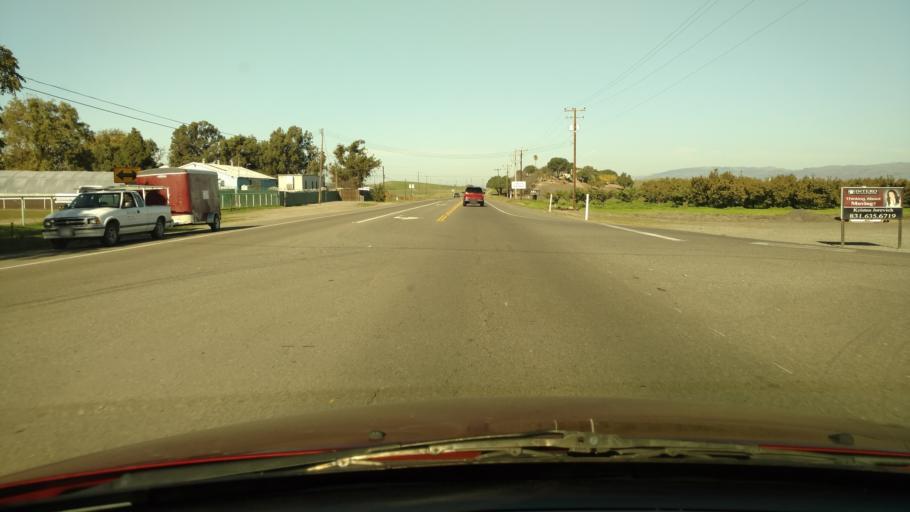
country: US
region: California
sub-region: San Benito County
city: Hollister
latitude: 36.8818
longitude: -121.4151
